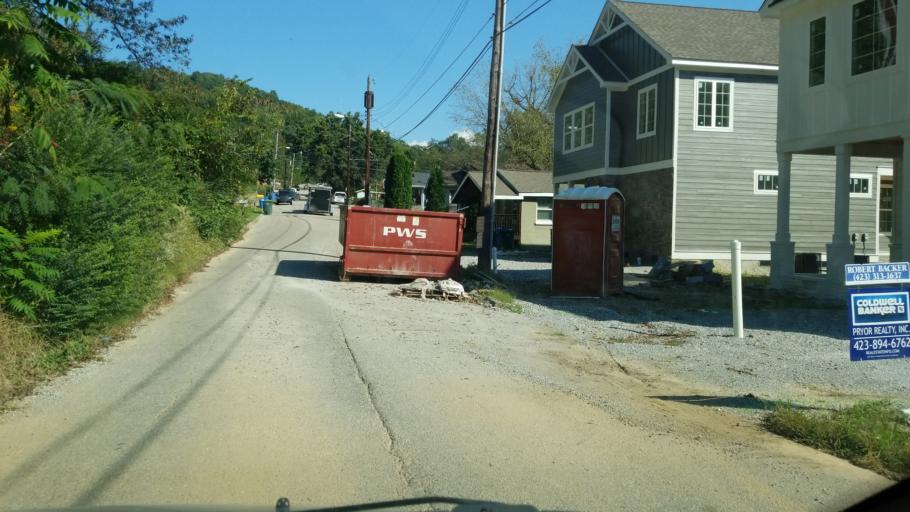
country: US
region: Tennessee
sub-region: Hamilton County
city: Chattanooga
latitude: 35.0710
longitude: -85.3121
